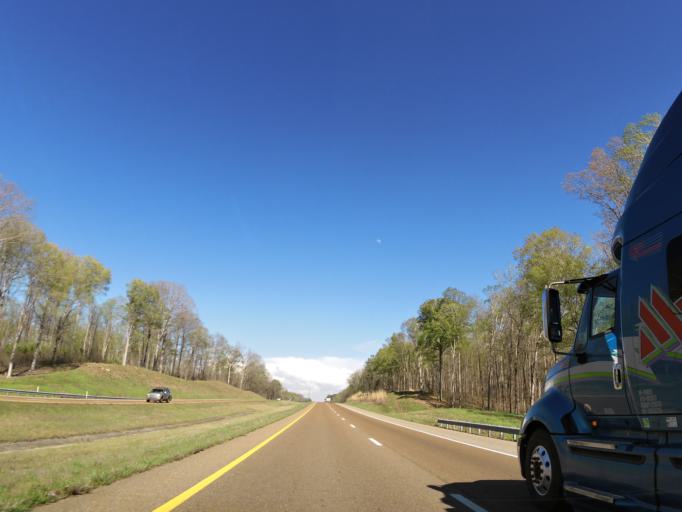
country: US
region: Tennessee
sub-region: Decatur County
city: Parsons
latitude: 35.8159
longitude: -88.1977
